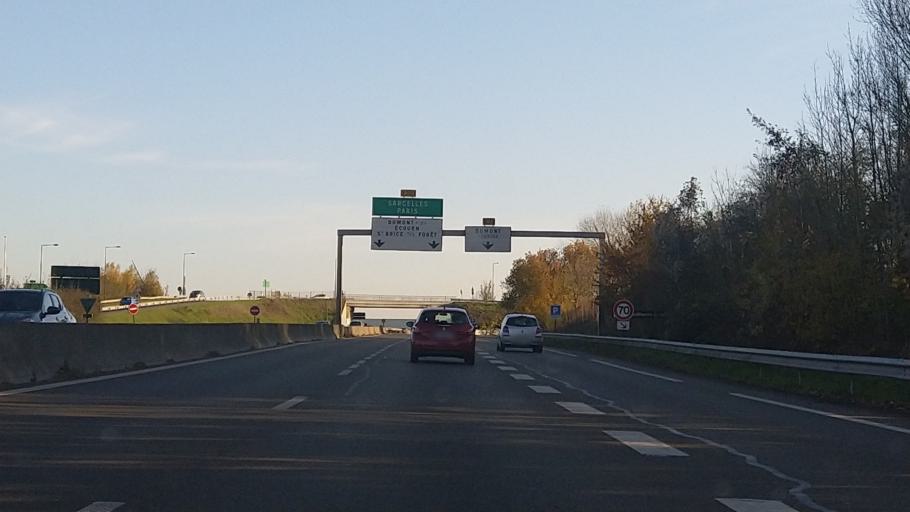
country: FR
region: Ile-de-France
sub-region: Departement du Val-d'Oise
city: Moisselles
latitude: 49.0453
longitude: 2.3355
